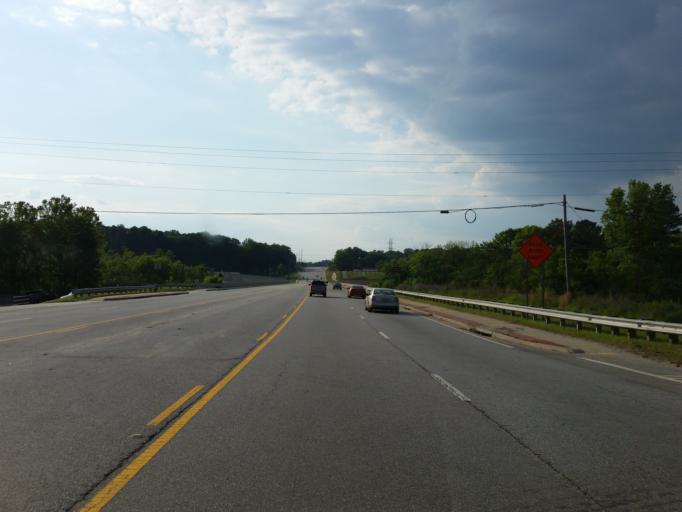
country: US
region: Georgia
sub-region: Cobb County
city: Vinings
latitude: 33.8159
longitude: -84.4783
